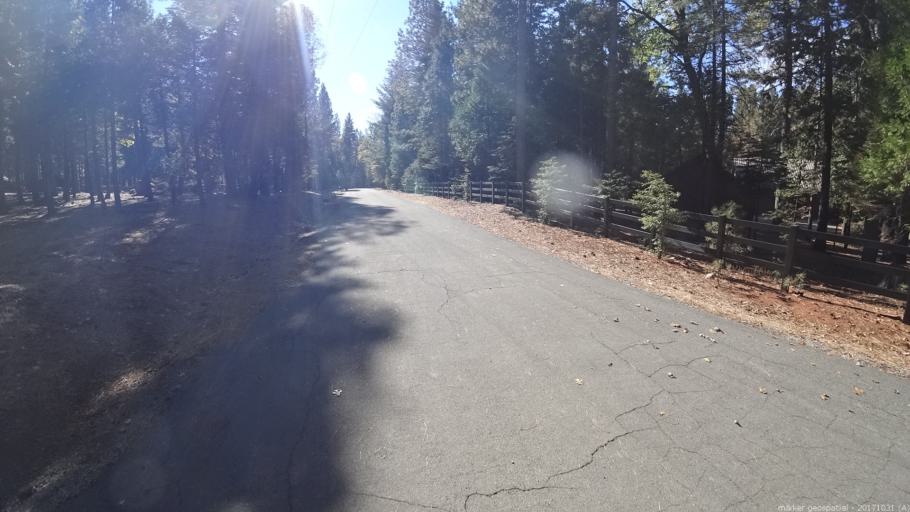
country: US
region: California
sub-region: Shasta County
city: Shingletown
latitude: 40.4865
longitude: -121.8943
